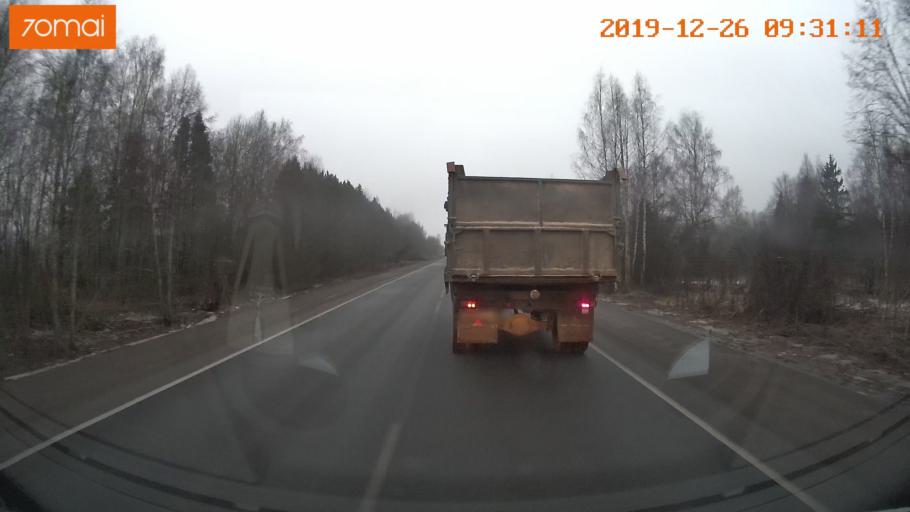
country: RU
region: Vologda
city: Gryazovets
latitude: 59.0672
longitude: 40.1305
